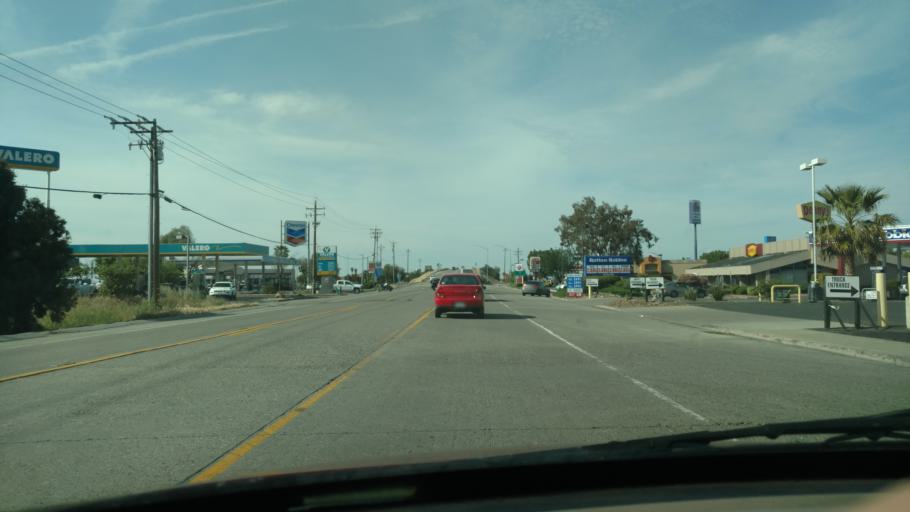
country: US
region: California
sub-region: Merced County
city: Gustine
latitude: 37.1022
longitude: -121.0158
